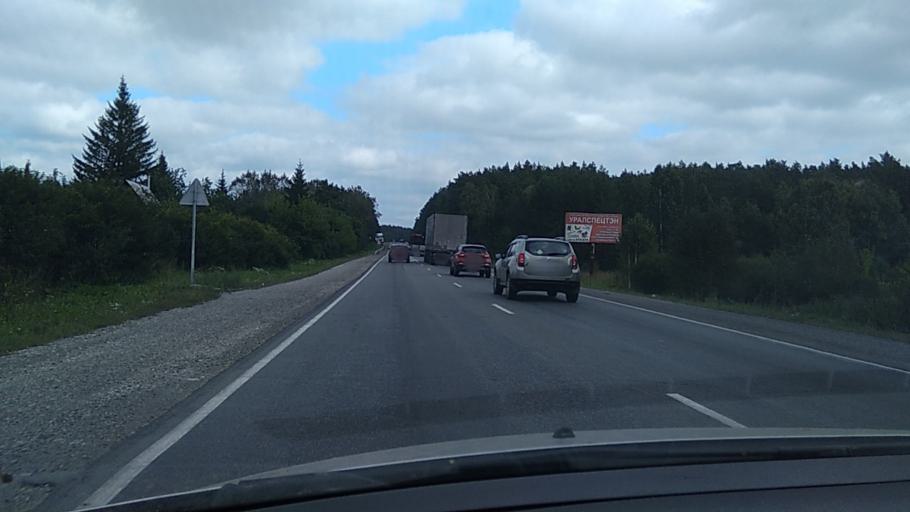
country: RU
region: Chelyabinsk
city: Miass
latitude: 54.9447
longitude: 60.0884
